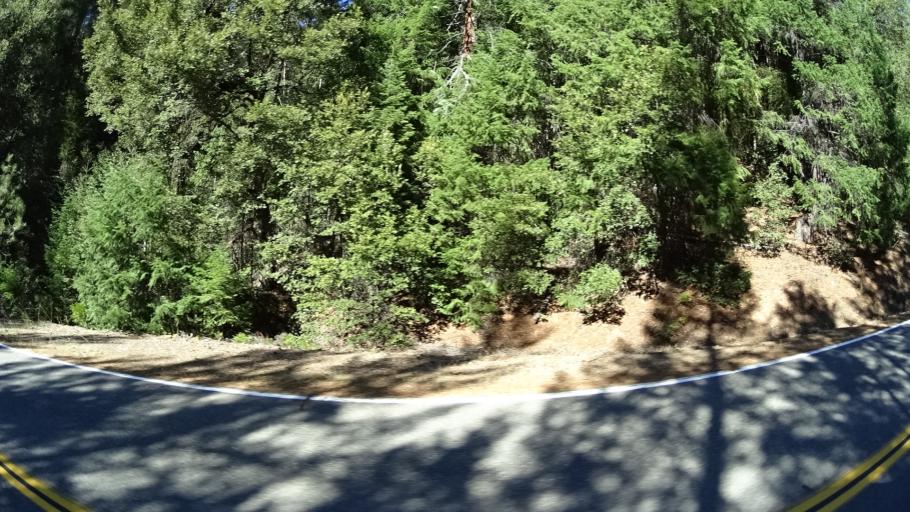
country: US
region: California
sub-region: Trinity County
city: Weaverville
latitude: 41.2267
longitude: -123.0177
